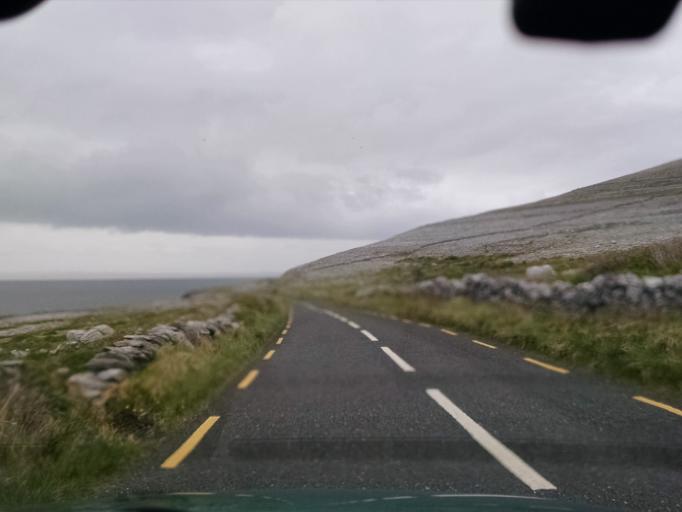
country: IE
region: Connaught
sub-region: County Galway
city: Bearna
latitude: 53.1442
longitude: -9.2735
